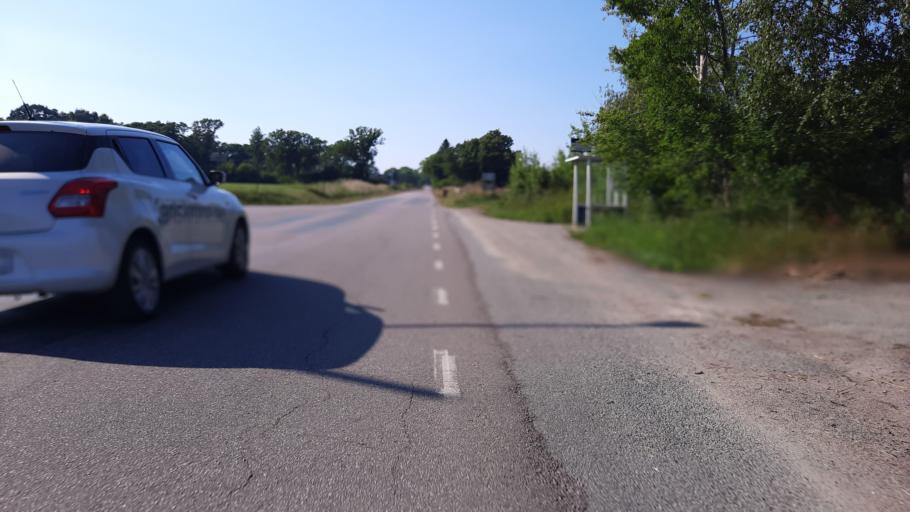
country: SE
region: Blekinge
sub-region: Karlskrona Kommun
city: Sturko
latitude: 56.1060
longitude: 15.6878
